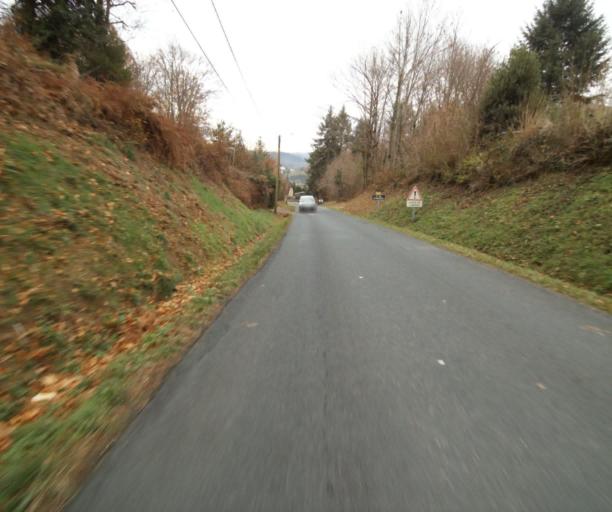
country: FR
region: Limousin
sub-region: Departement de la Correze
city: Tulle
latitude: 45.2617
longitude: 1.7356
